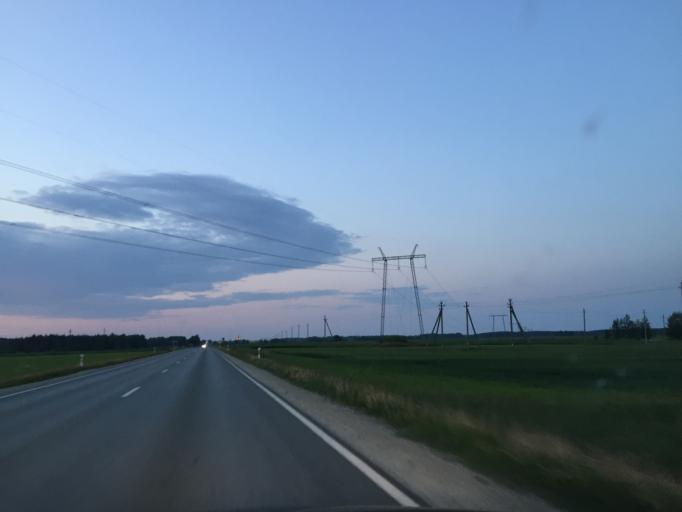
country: LT
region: Siauliu apskritis
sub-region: Joniskis
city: Joniskis
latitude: 56.1077
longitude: 23.4865
